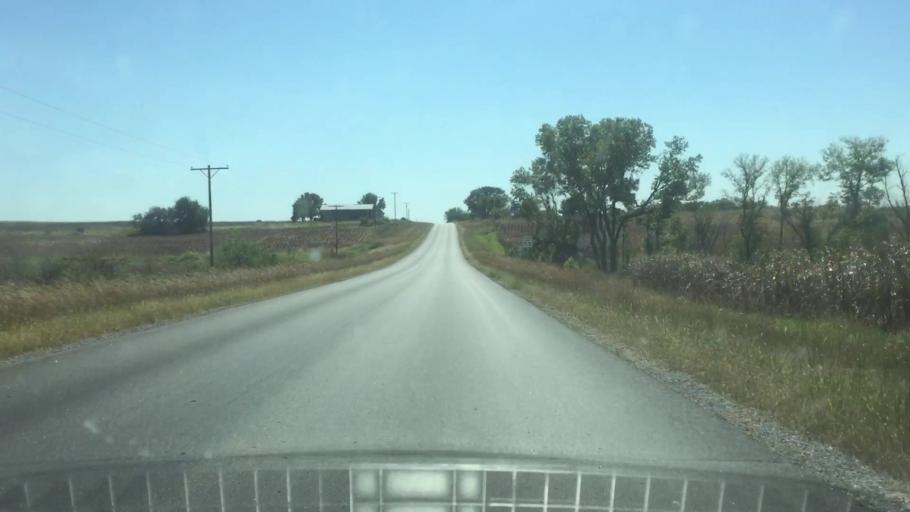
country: US
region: Kansas
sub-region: Marshall County
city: Marysville
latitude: 39.9566
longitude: -96.6009
